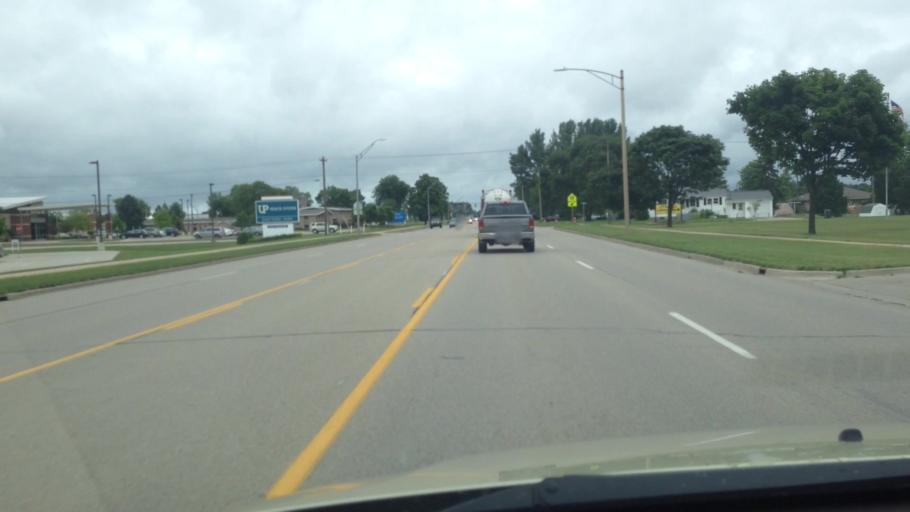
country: US
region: Michigan
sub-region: Delta County
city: Escanaba
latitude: 45.7362
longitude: -87.0799
